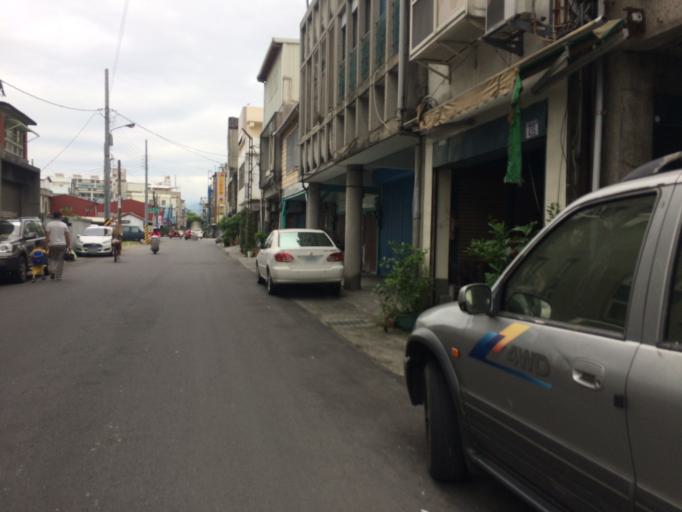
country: TW
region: Taiwan
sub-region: Hualien
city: Hualian
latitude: 23.9743
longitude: 121.6087
